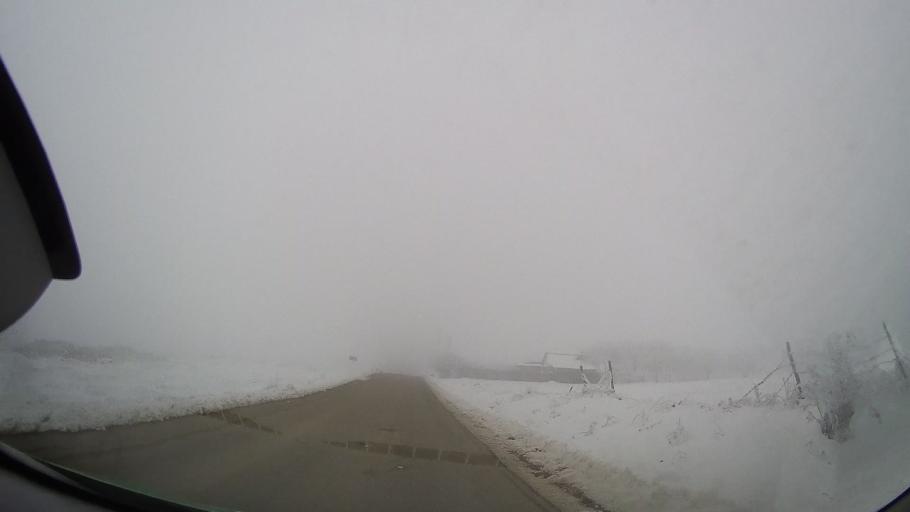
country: RO
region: Iasi
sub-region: Comuna Tansa
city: Suhulet
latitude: 46.8940
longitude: 27.2676
